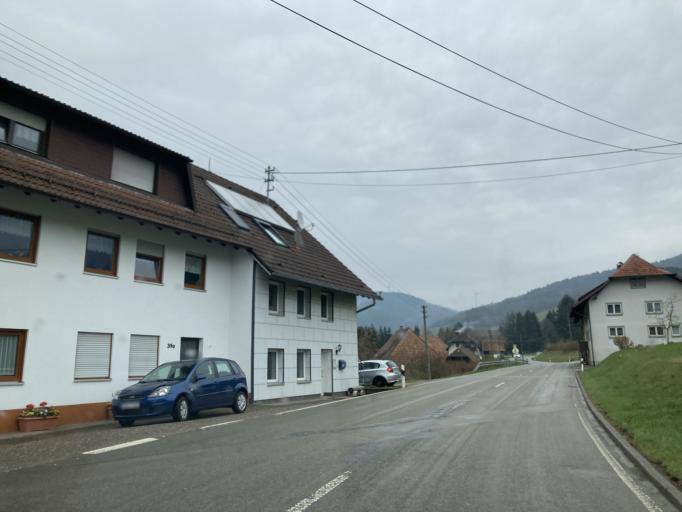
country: DE
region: Baden-Wuerttemberg
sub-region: Freiburg Region
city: Muhlenbach
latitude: 48.2058
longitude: 8.1220
